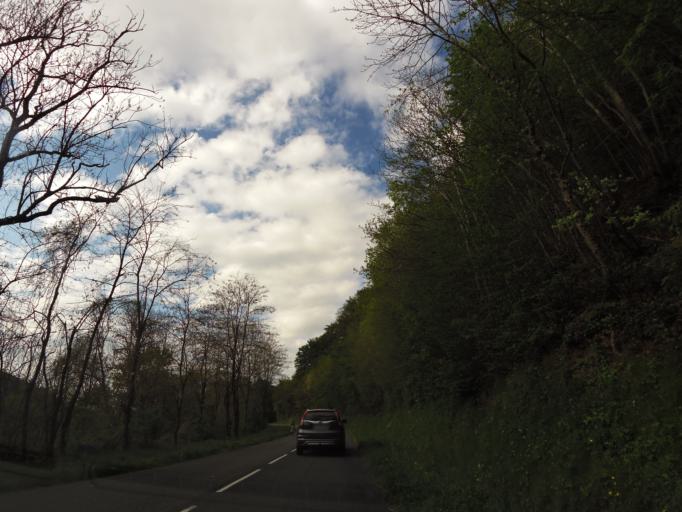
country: FR
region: Midi-Pyrenees
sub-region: Departement du Tarn
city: Soreze
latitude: 43.4248
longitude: 2.0568
